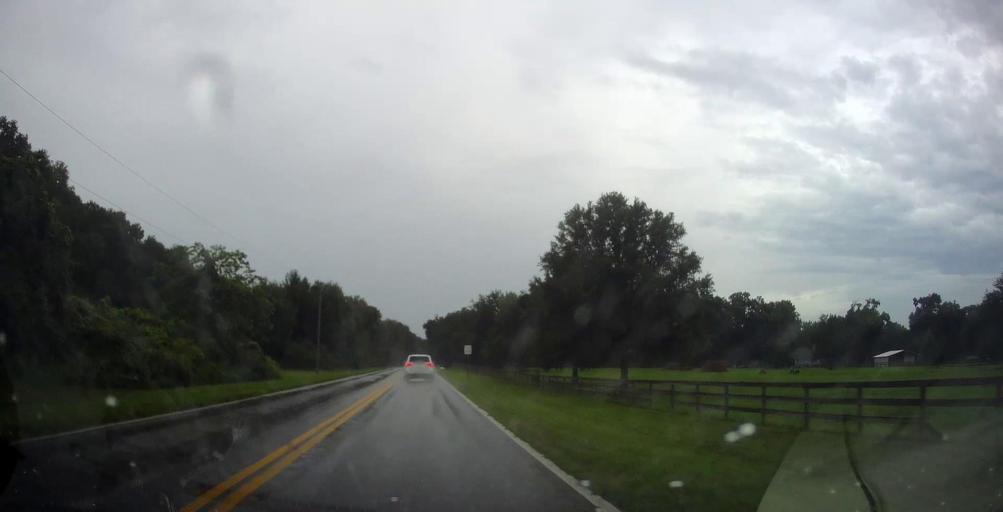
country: US
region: Florida
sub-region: Marion County
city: Ocala
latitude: 29.2520
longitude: -82.0908
